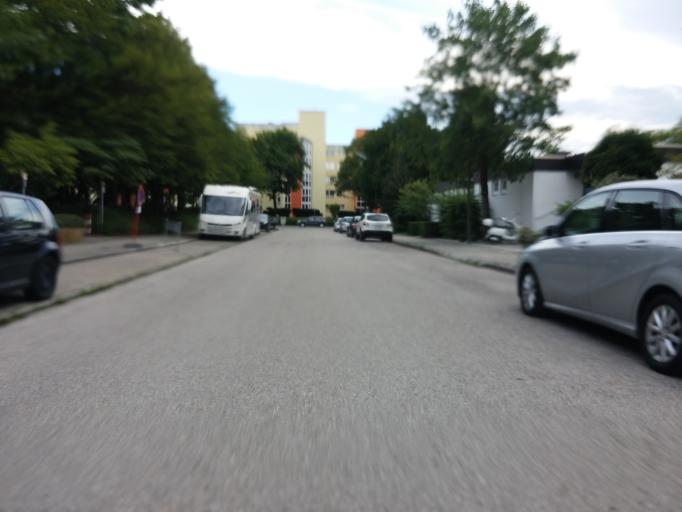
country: DE
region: Bavaria
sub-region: Upper Bavaria
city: Haar
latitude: 48.1073
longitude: 11.7186
